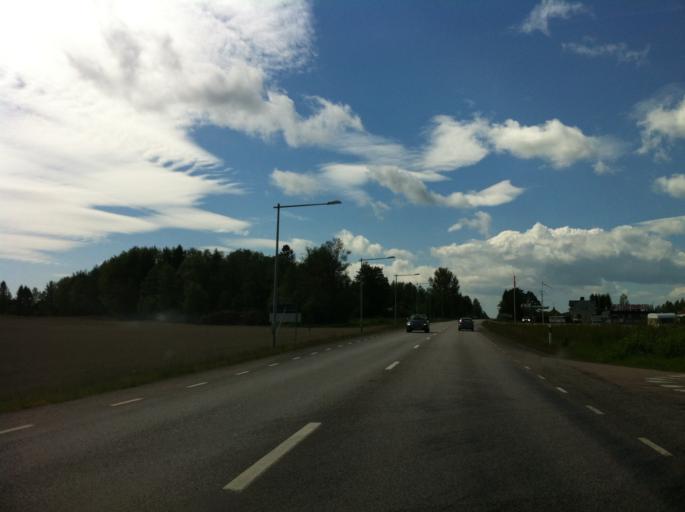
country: SE
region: Vaermland
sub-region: Saffle Kommun
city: Saeffle
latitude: 59.1909
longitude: 13.0197
